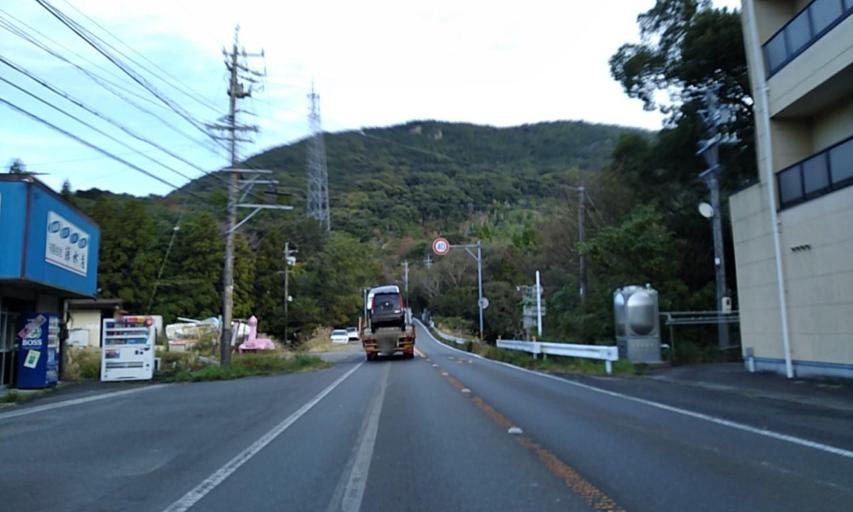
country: JP
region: Mie
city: Toba
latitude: 34.3946
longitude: 136.7871
